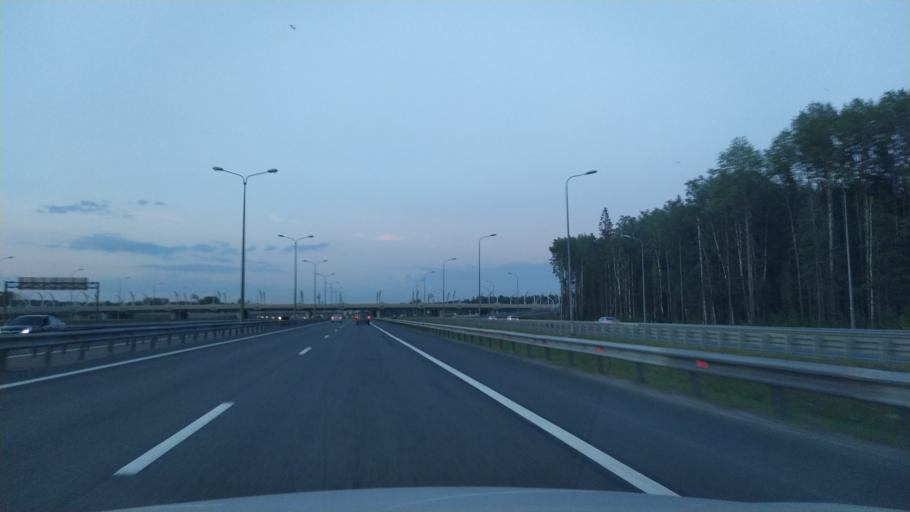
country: RU
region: St.-Petersburg
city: Ol'gino
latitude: 60.0576
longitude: 30.1362
